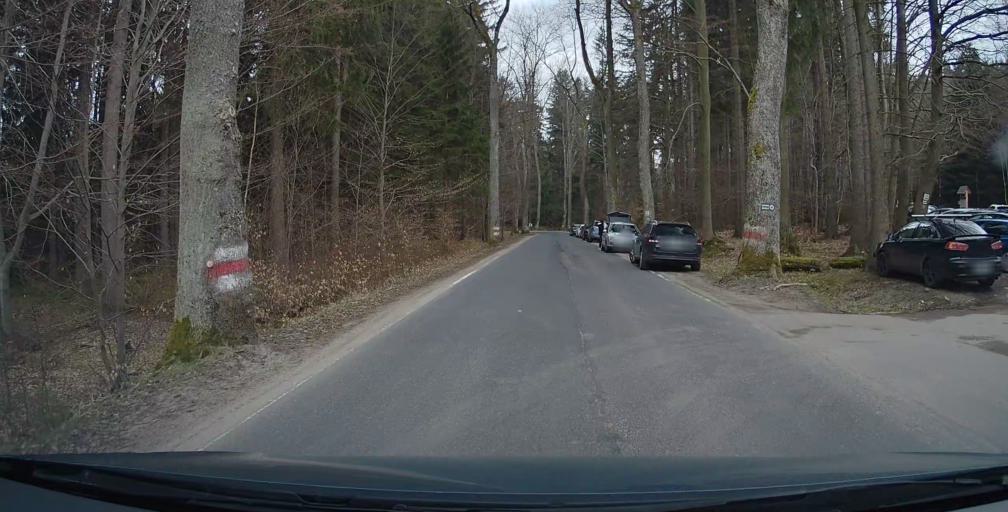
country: PL
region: Lower Silesian Voivodeship
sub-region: Powiat klodzki
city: Radkow
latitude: 50.4760
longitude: 16.3873
